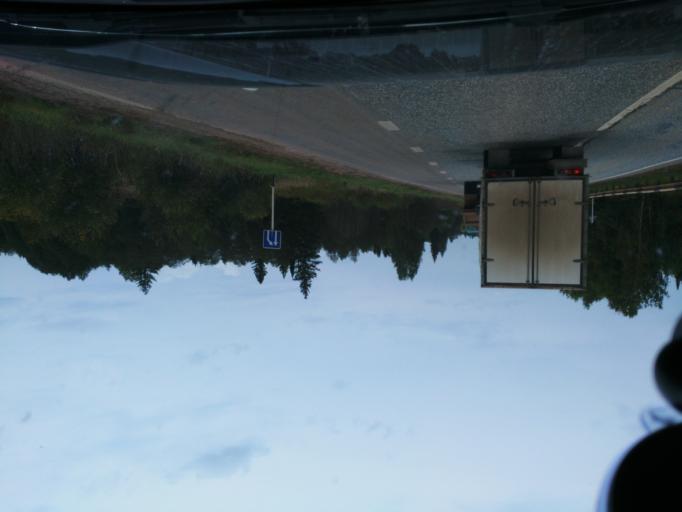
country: RU
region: Perm
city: Chernushka
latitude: 56.5023
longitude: 55.8681
